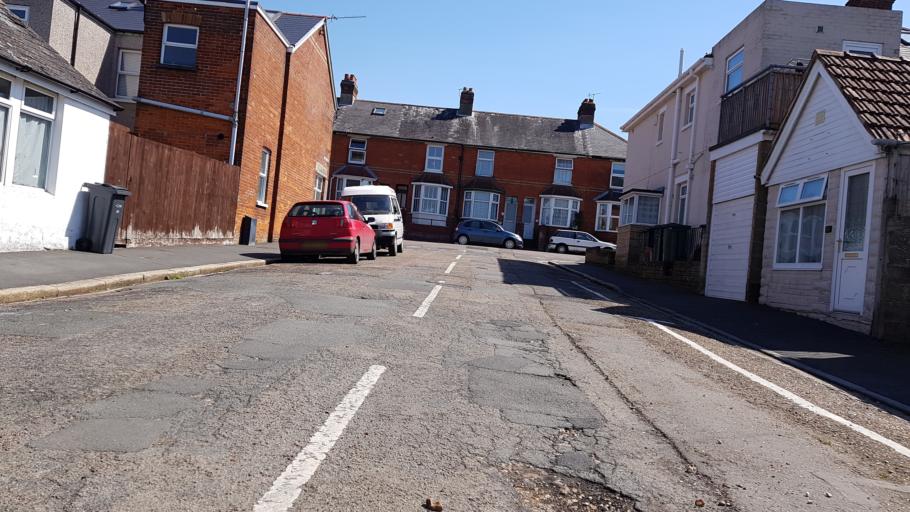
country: GB
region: England
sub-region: Isle of Wight
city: East Cowes
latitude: 50.7538
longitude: -1.2840
